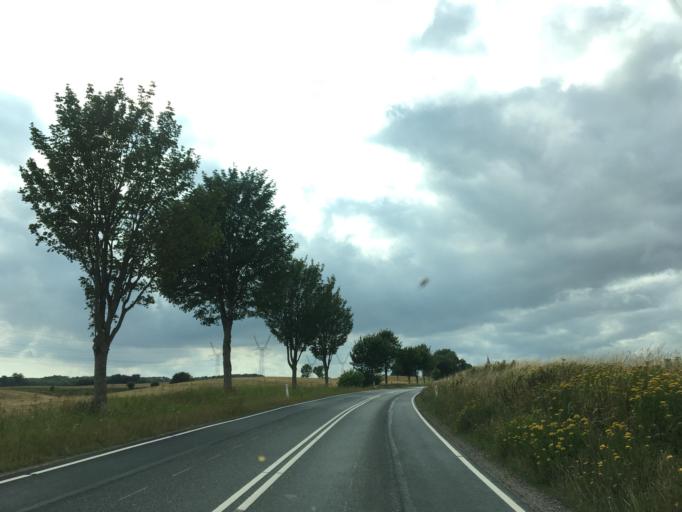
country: DK
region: South Denmark
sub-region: Assens Kommune
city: Arup
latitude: 55.4138
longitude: 10.0361
